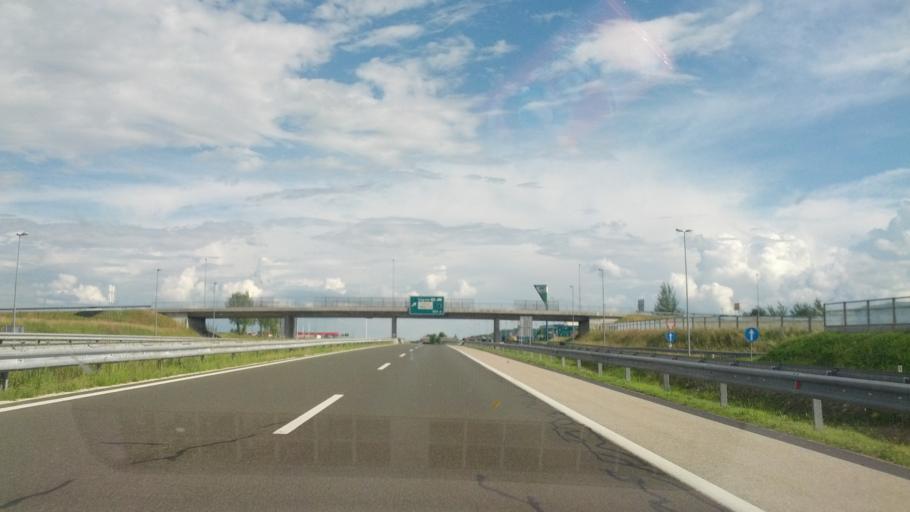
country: HR
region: Zagrebacka
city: Bregana
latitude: 45.8580
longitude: 15.6834
